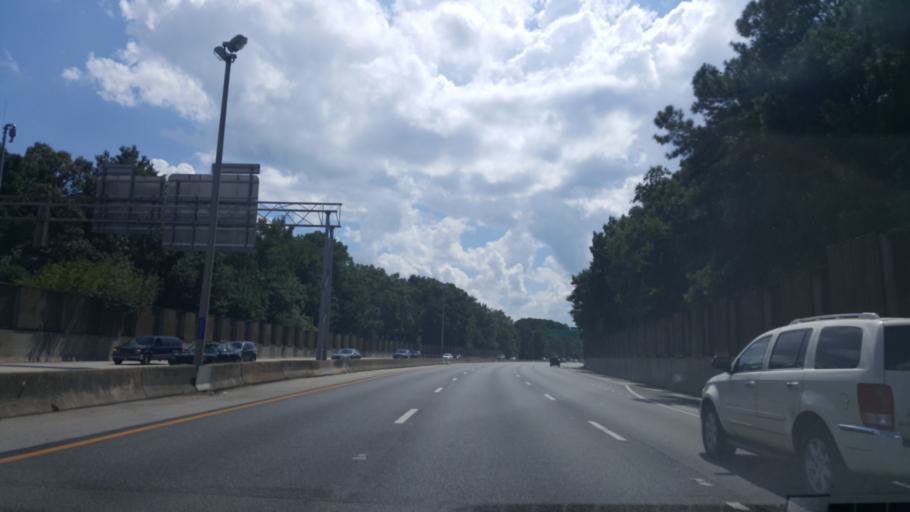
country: US
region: Virginia
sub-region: City of Hampton
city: Hampton
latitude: 37.0199
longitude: -76.3826
